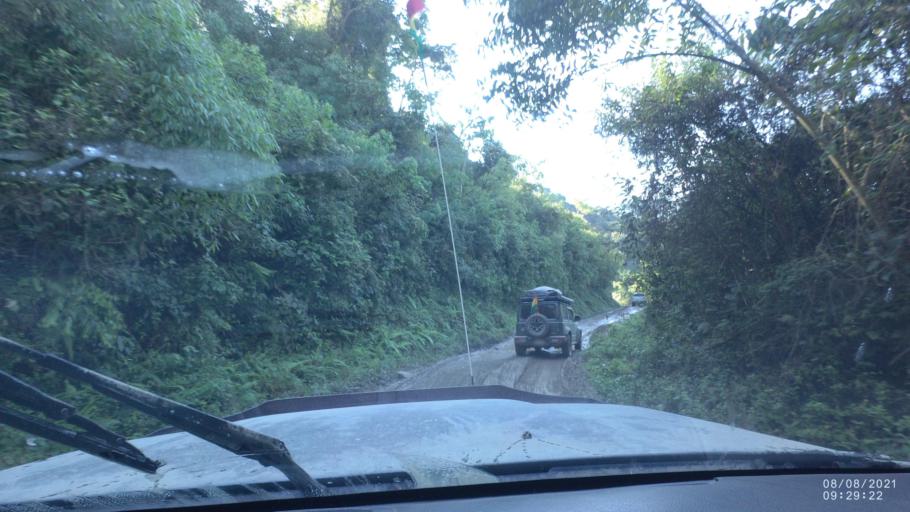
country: BO
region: La Paz
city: Quime
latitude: -16.5860
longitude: -66.7119
